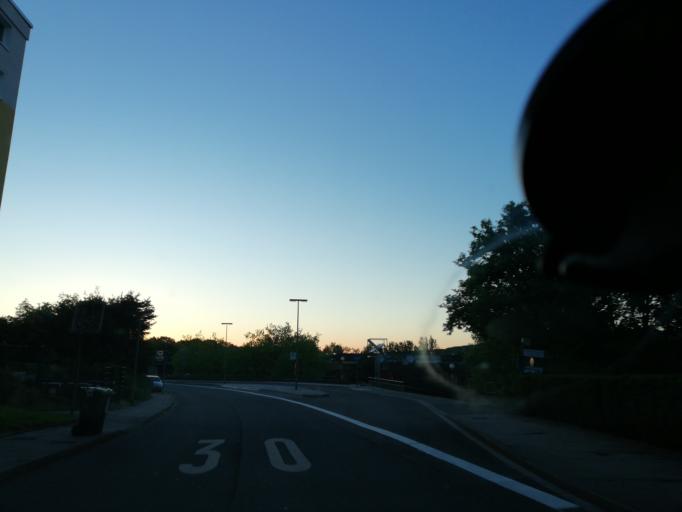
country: DE
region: North Rhine-Westphalia
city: Wetter (Ruhr)
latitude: 51.3845
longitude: 7.3770
